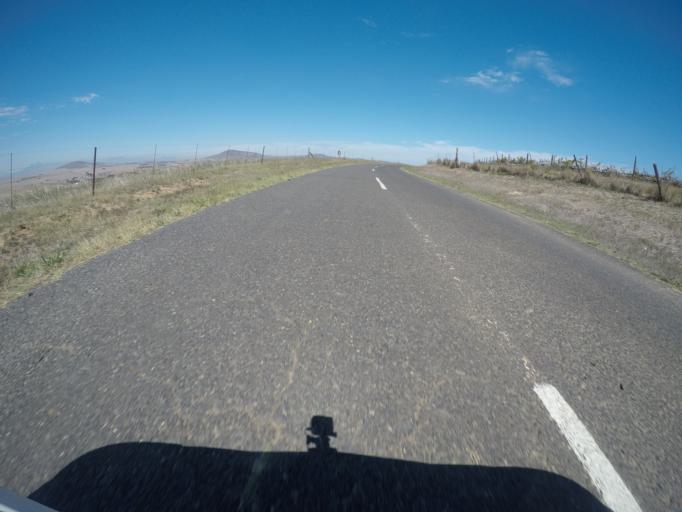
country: ZA
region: Western Cape
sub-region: City of Cape Town
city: Sunset Beach
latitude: -33.7148
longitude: 18.5826
